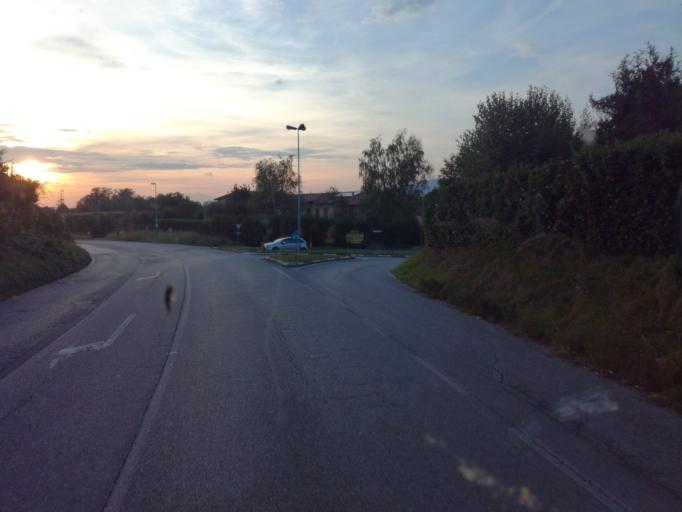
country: IT
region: Lombardy
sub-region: Provincia di Lecco
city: Barzago
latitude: 45.7553
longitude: 9.3088
